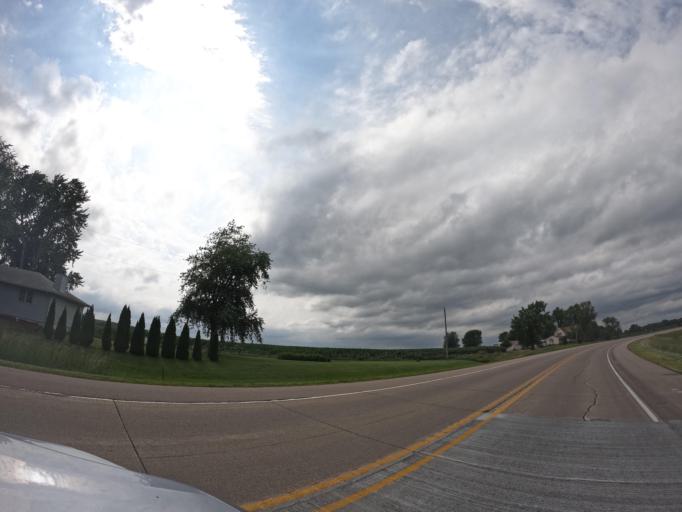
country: US
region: Iowa
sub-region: Clinton County
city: De Witt
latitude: 41.7840
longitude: -90.5405
